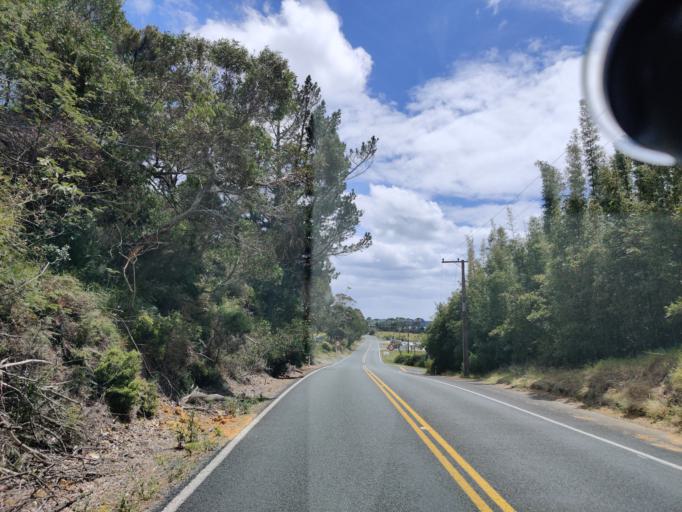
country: NZ
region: Northland
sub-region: Far North District
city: Kaitaia
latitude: -34.8090
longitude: 173.1156
